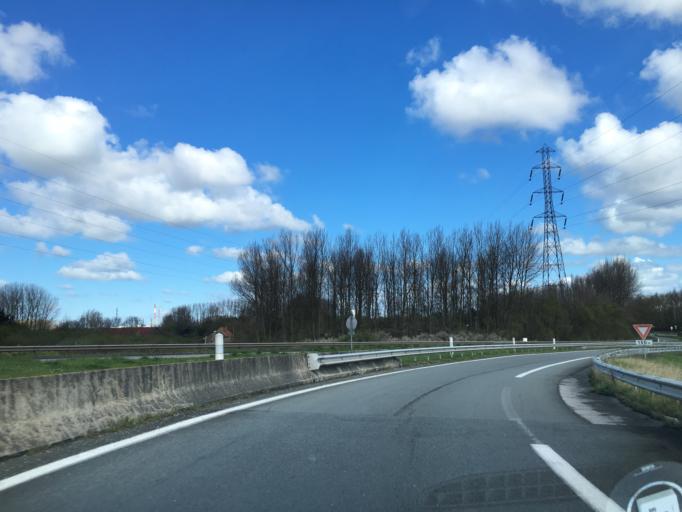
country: FR
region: Nord-Pas-de-Calais
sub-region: Departement du Nord
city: Grande-Synthe
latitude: 50.9996
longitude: 2.2889
